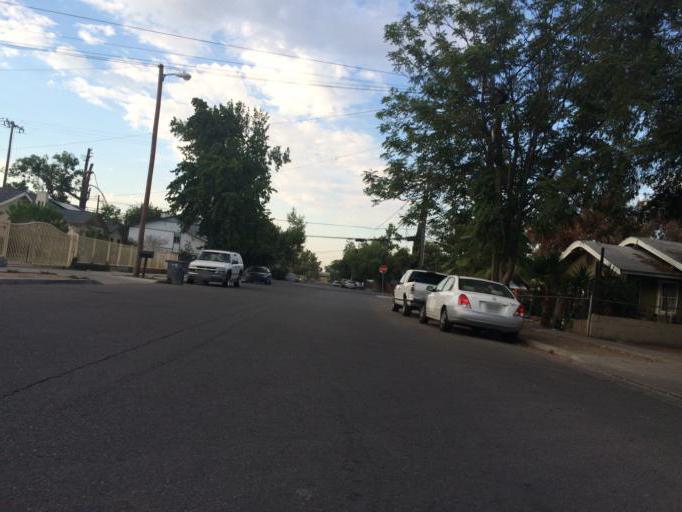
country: US
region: California
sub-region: Fresno County
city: Fresno
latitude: 36.7585
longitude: -119.7613
